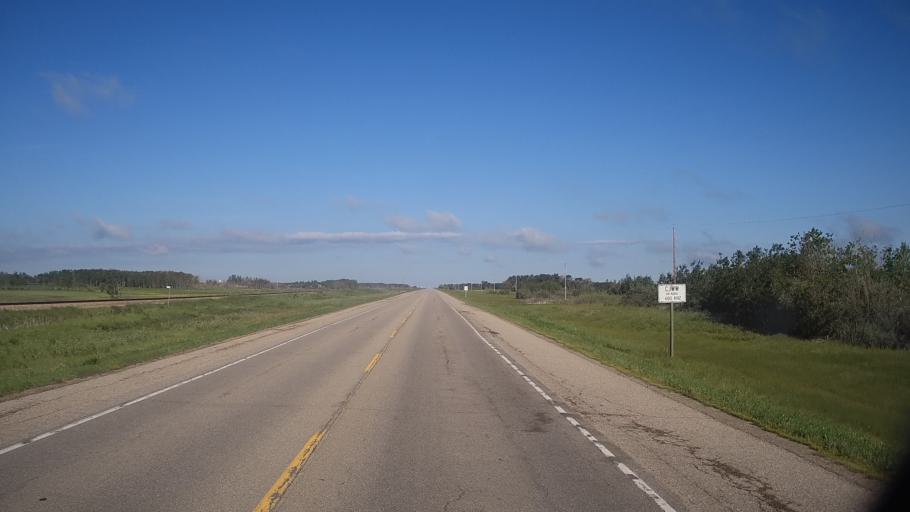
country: CA
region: Saskatchewan
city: Lanigan
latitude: 51.8511
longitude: -105.0650
